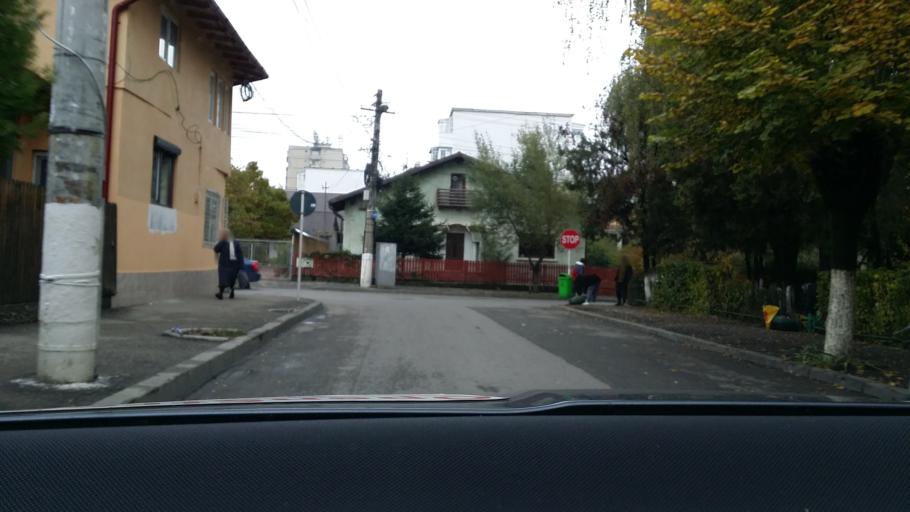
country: RO
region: Prahova
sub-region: Municipiul Campina
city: Campina
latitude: 45.1264
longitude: 25.7395
